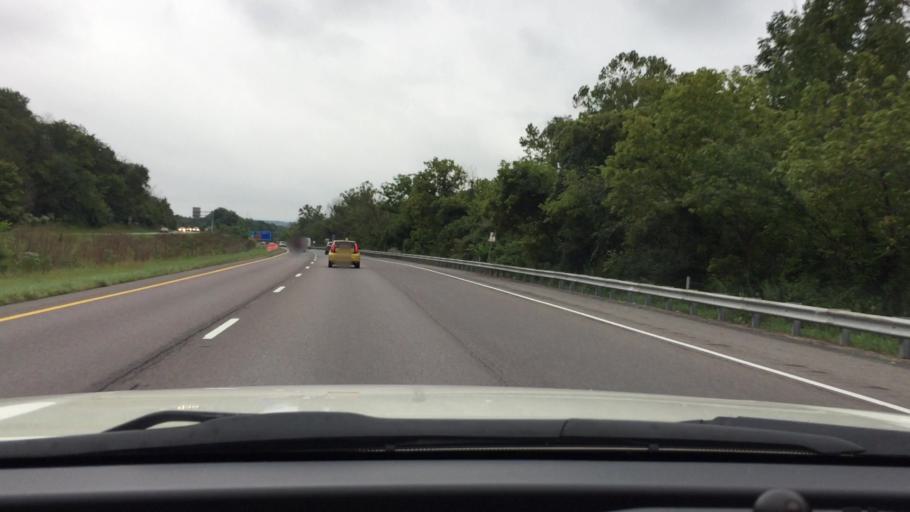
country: US
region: Maryland
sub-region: Washington County
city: Hancock
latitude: 39.6933
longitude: -78.1430
